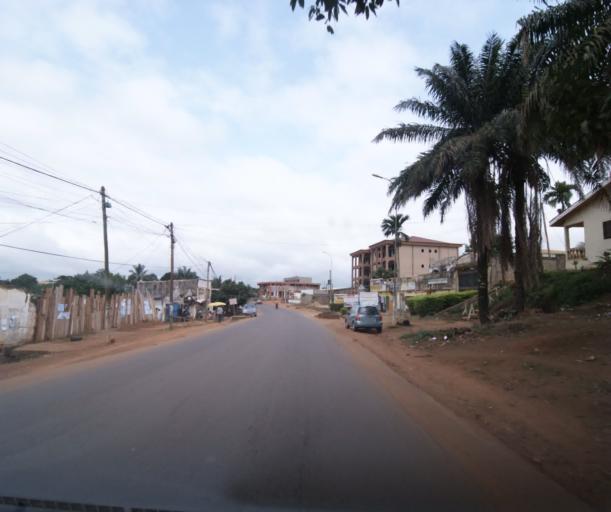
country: CM
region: Centre
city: Yaounde
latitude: 3.8011
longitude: 11.5254
